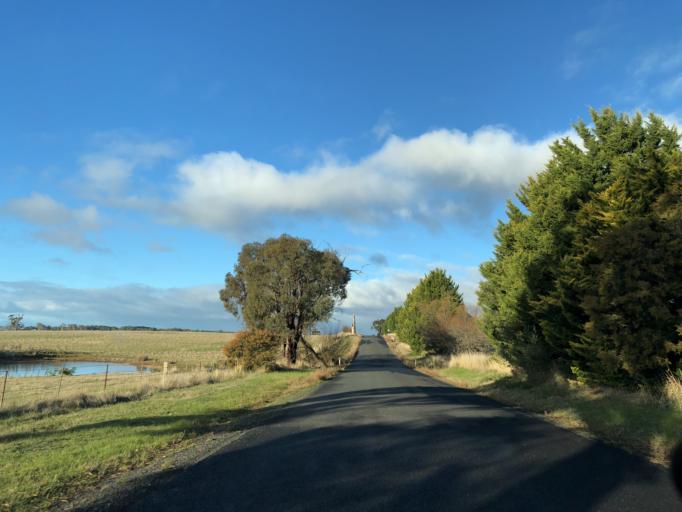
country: AU
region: Victoria
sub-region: Mount Alexander
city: Castlemaine
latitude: -37.2116
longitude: 144.3194
